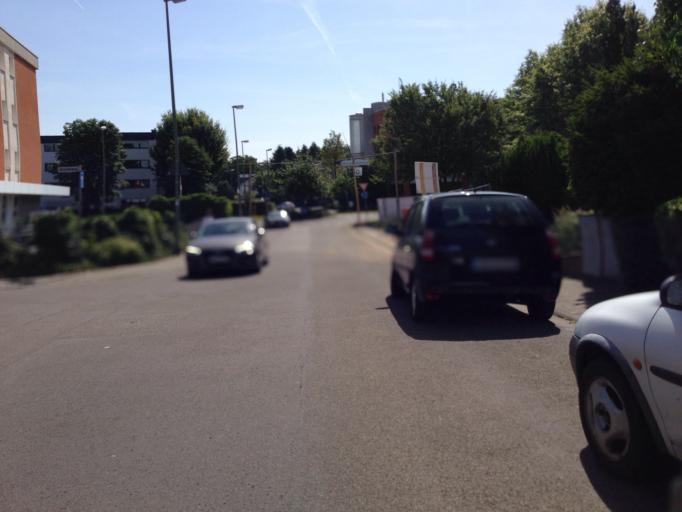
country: DE
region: Hesse
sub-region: Regierungsbezirk Darmstadt
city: Hanau am Main
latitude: 50.1116
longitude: 8.9007
